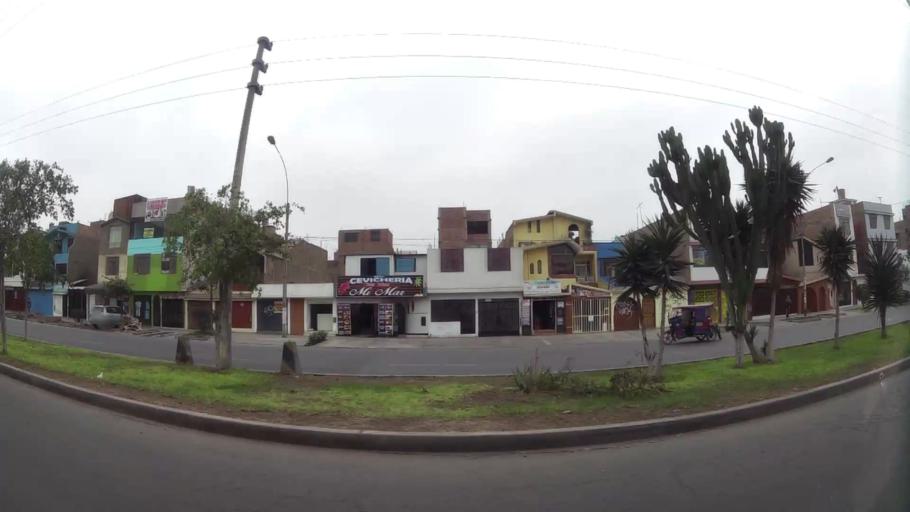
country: PE
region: Lima
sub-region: Lima
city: Independencia
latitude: -11.9452
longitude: -77.0775
